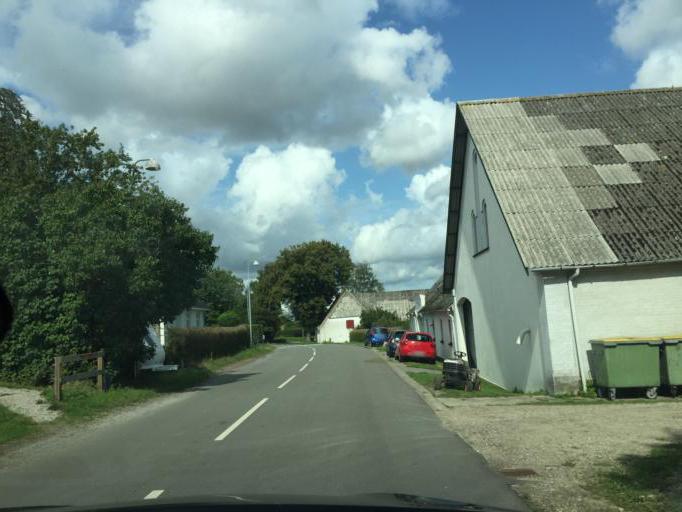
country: DK
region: South Denmark
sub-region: Odense Kommune
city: Stige
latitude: 55.4619
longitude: 10.3759
